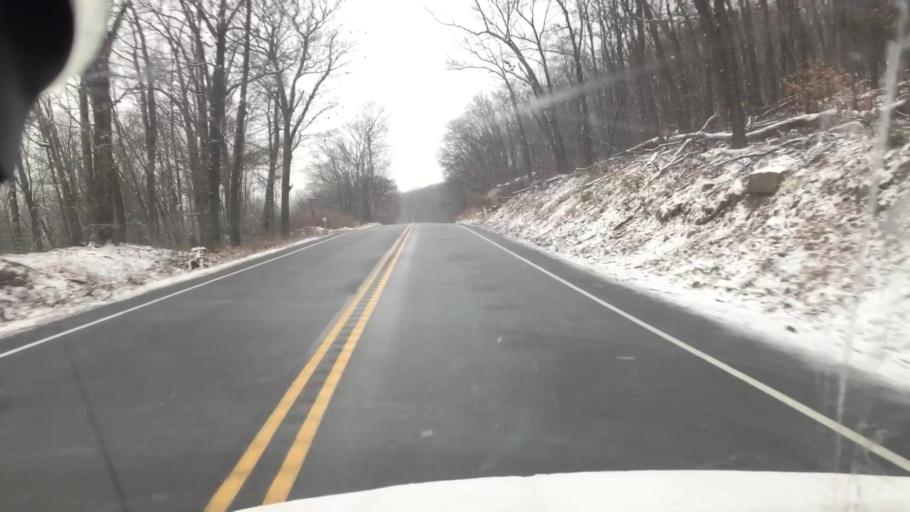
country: US
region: Pennsylvania
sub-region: Luzerne County
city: Conyngham
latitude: 41.0312
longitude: -76.0891
